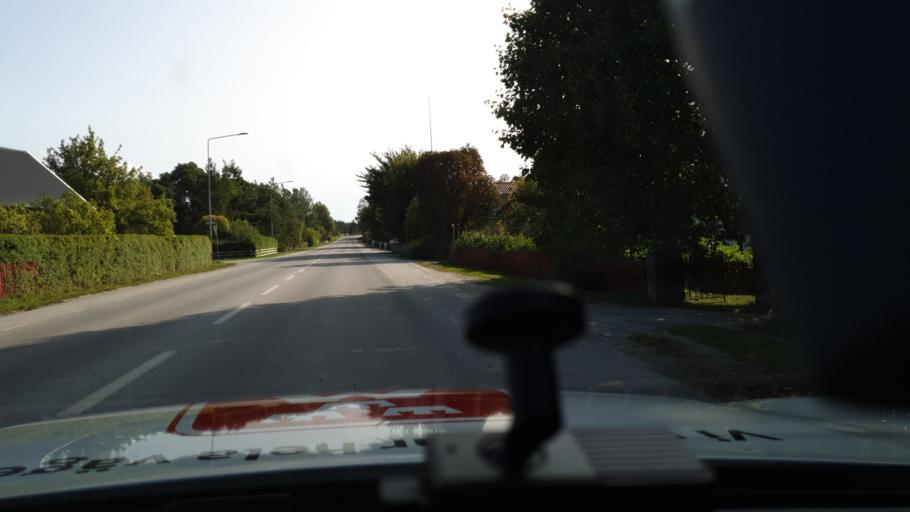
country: SE
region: Gotland
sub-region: Gotland
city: Slite
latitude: 57.7197
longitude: 18.7909
